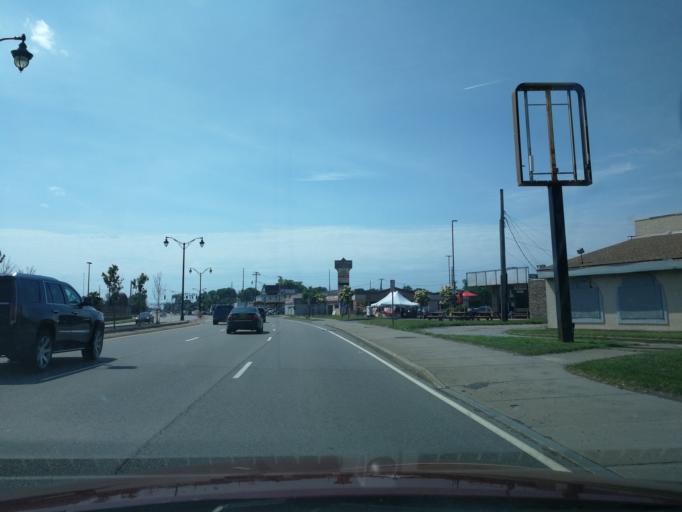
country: US
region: New York
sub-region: Monroe County
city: Greece
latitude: 43.2021
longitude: -77.6428
